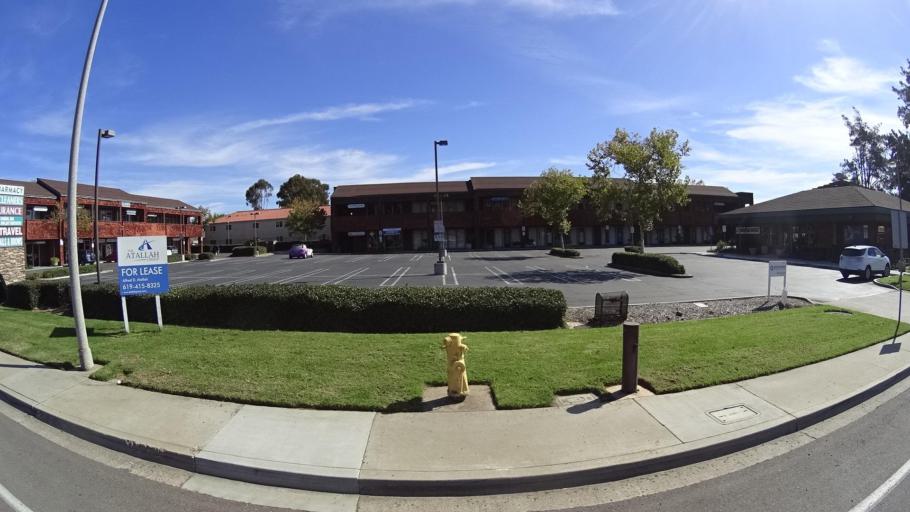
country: US
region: California
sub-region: San Diego County
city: Casa de Oro-Mount Helix
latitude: 32.7488
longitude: -116.9620
